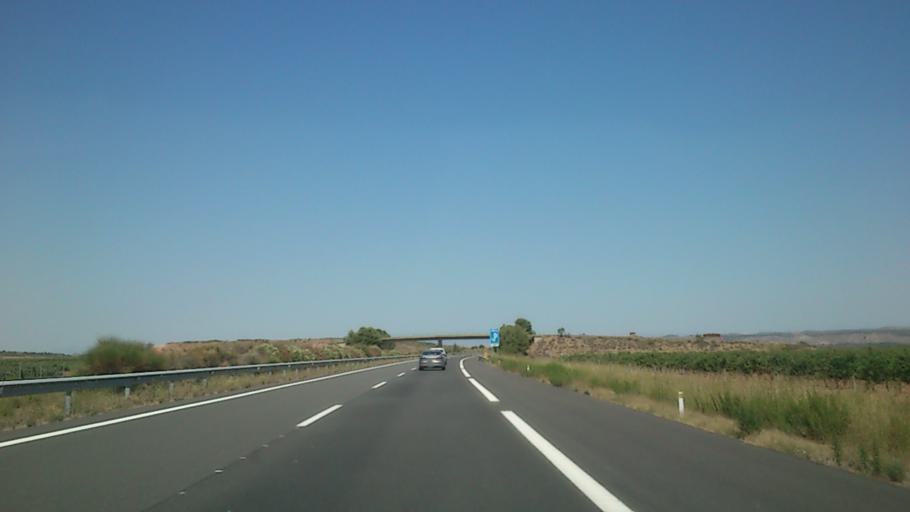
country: ES
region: La Rioja
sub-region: Provincia de La Rioja
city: Aldeanueva de Ebro
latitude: 42.2282
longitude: -1.8994
